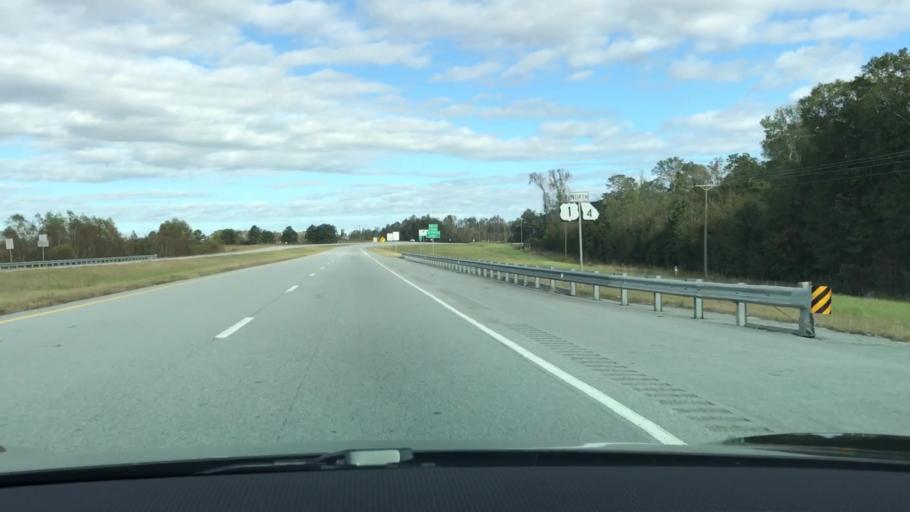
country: US
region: Georgia
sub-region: Jefferson County
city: Wadley
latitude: 32.8136
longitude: -82.4038
